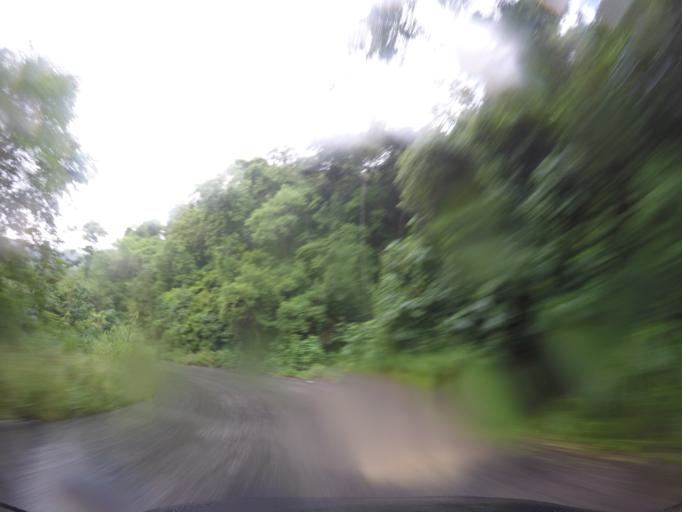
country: MX
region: Oaxaca
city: San Gabriel Mixtepec
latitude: 16.0578
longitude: -97.0783
